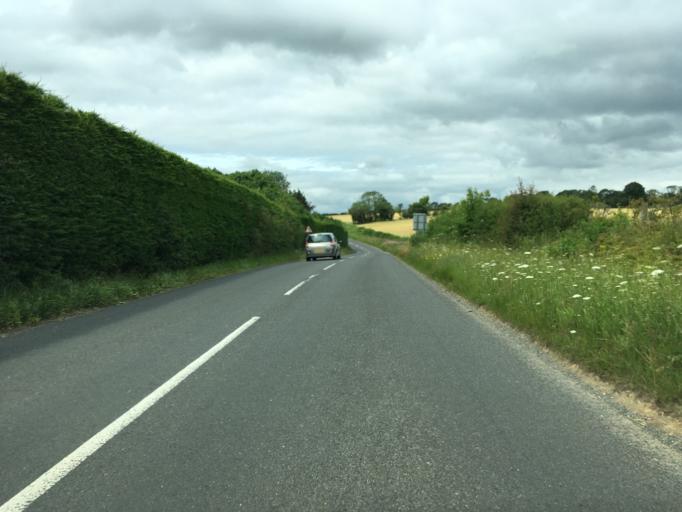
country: GB
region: England
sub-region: Gloucestershire
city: Stow on the Wold
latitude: 51.8820
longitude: -1.6955
